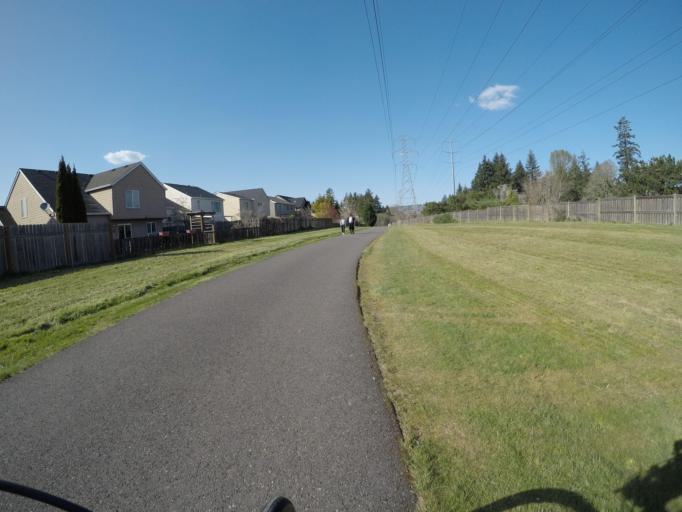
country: US
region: Oregon
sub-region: Washington County
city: Oak Hills
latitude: 45.5531
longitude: -122.8473
